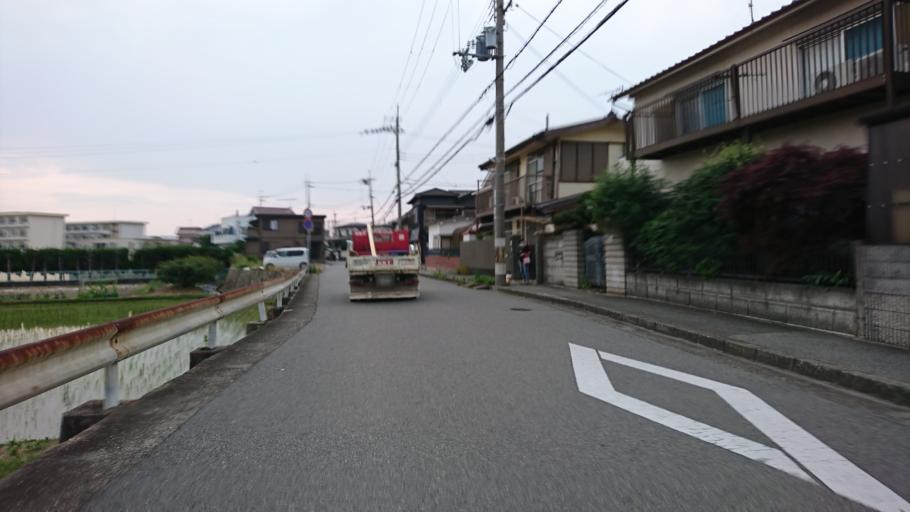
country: JP
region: Hyogo
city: Kakogawacho-honmachi
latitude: 34.7595
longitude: 134.8729
